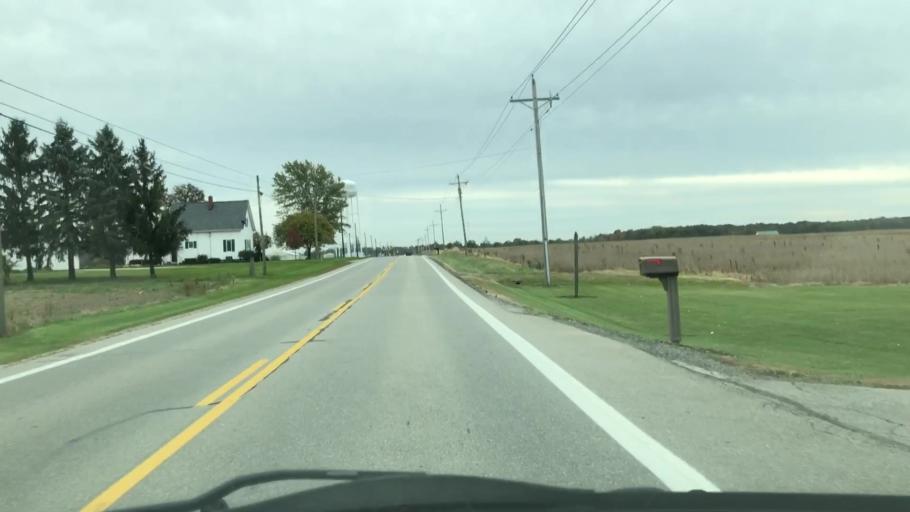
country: US
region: Ohio
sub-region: Williams County
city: Edgerton
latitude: 41.5766
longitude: -84.7692
